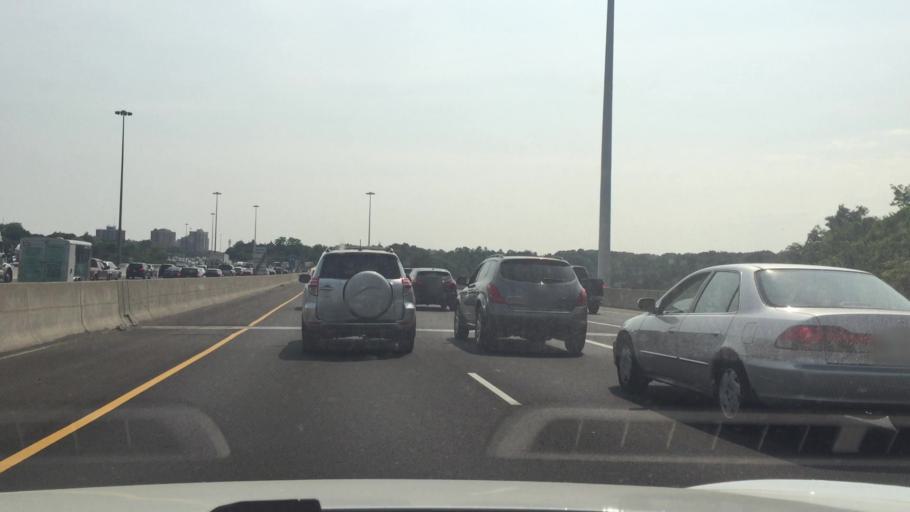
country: CA
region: Ontario
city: North York
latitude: 43.7528
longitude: -79.4105
